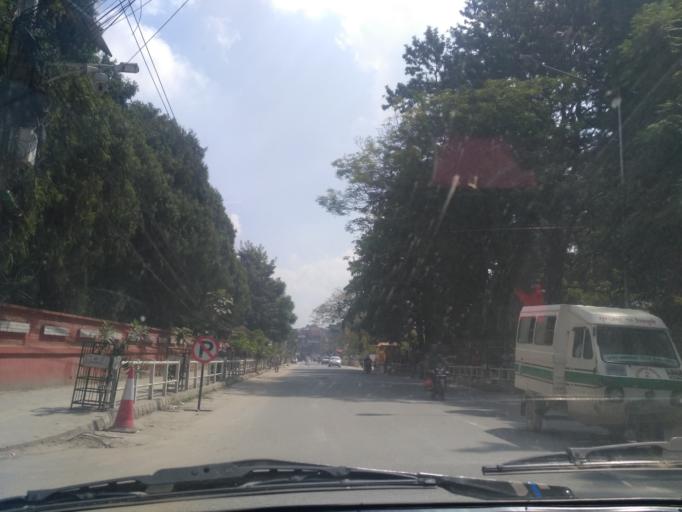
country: NP
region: Central Region
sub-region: Bagmati Zone
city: Kathmandu
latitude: 27.7022
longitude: 85.3184
